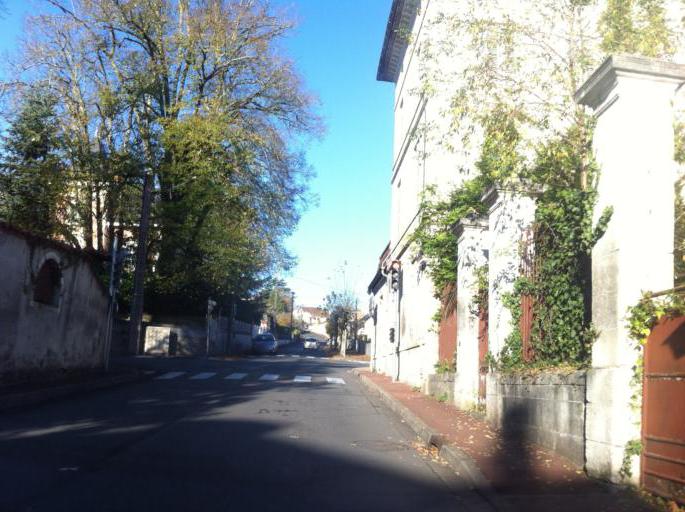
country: FR
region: Aquitaine
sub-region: Departement de la Dordogne
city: Riberac
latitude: 45.2478
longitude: 0.3381
